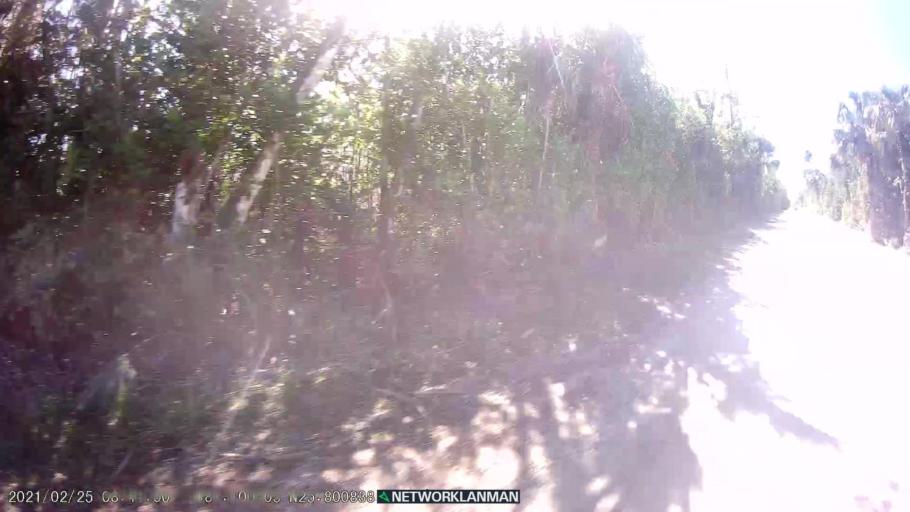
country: US
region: Florida
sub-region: Collier County
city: Marco
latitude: 25.8007
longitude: -81.1005
